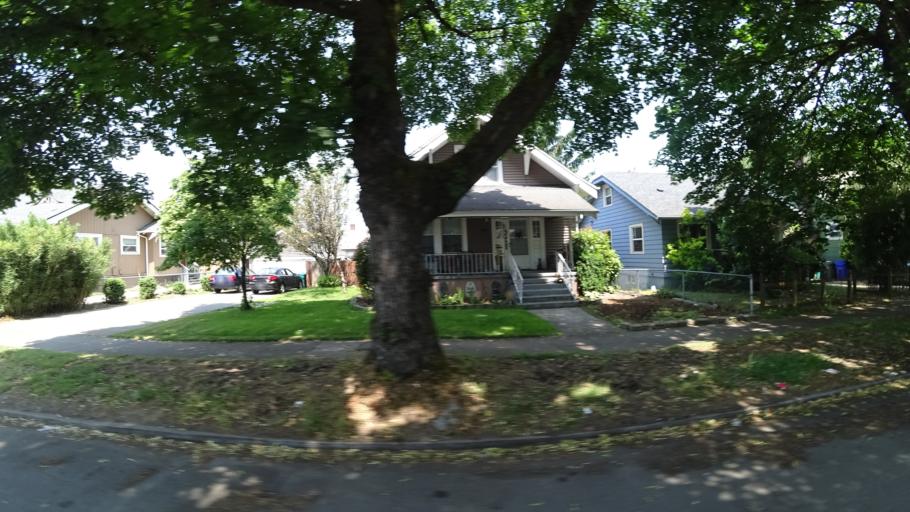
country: US
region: Oregon
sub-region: Multnomah County
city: Portland
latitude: 45.5772
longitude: -122.6739
